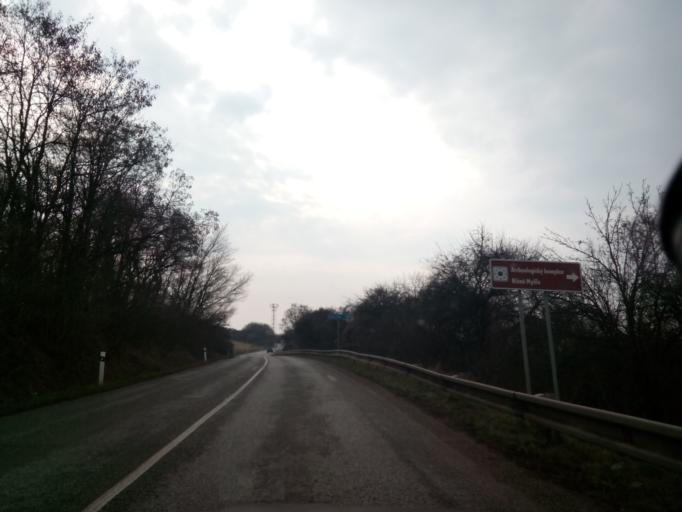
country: SK
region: Kosicky
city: Kosice
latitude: 48.6445
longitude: 21.3666
